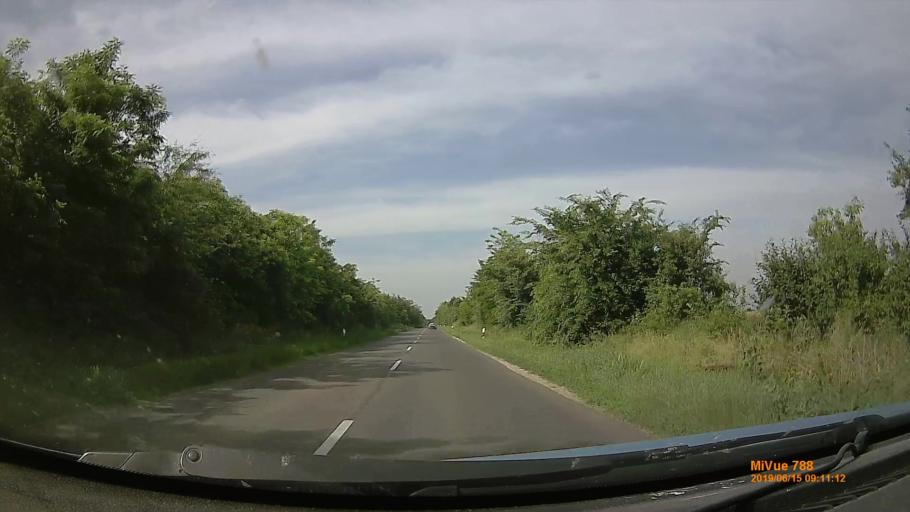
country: HU
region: Tolna
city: Iregszemcse
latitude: 46.6802
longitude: 18.1847
